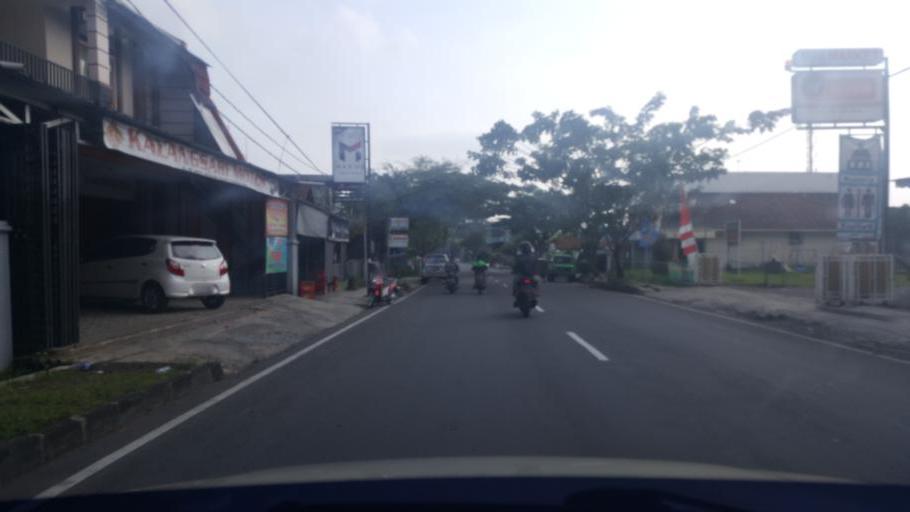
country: ID
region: West Java
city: Cibogor
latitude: -7.3170
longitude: 108.2282
